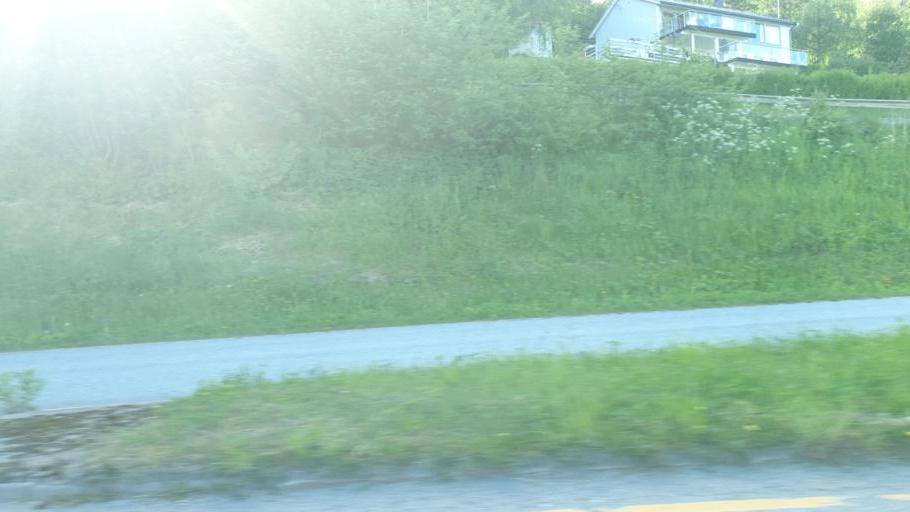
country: NO
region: Sor-Trondelag
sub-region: Rissa
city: Rissa
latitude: 63.5076
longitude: 10.1317
